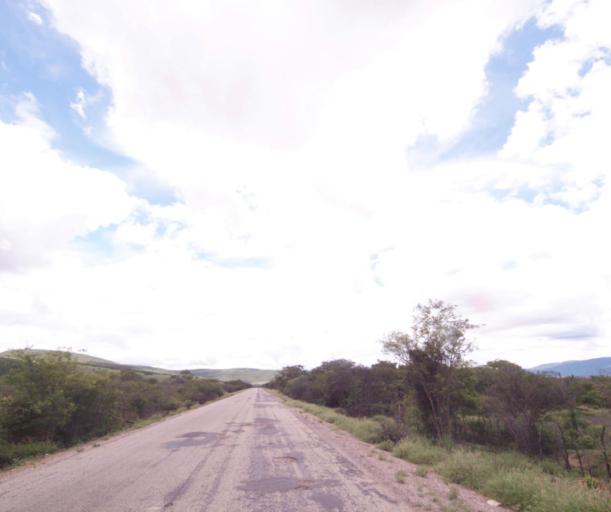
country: BR
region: Bahia
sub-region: Brumado
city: Brumado
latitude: -14.1841
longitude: -41.5719
